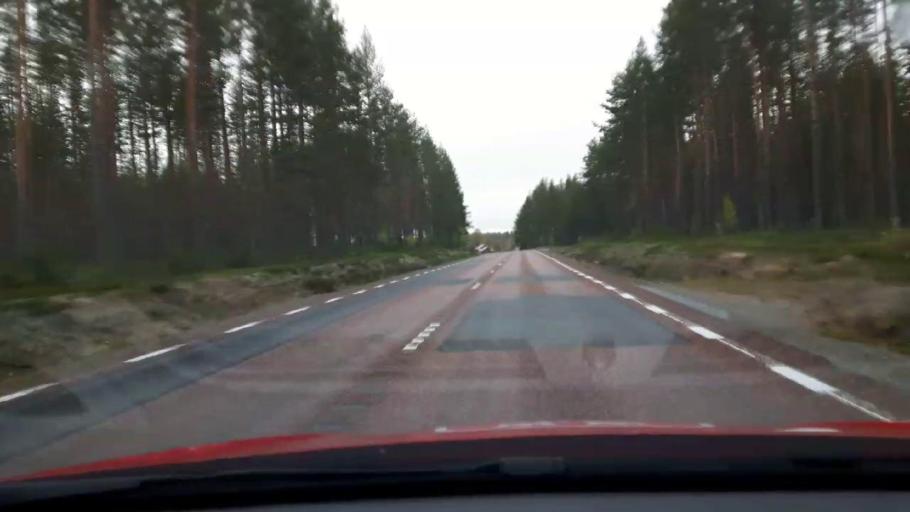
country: SE
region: Gaevleborg
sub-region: Ljusdals Kommun
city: Farila
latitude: 61.8447
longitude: 15.7509
